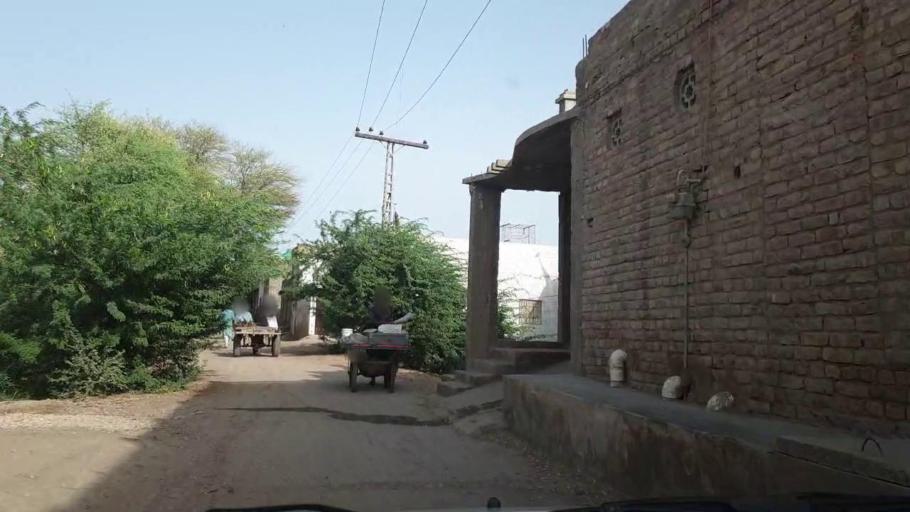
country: PK
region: Sindh
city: Nawabshah
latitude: 26.2333
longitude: 68.4058
